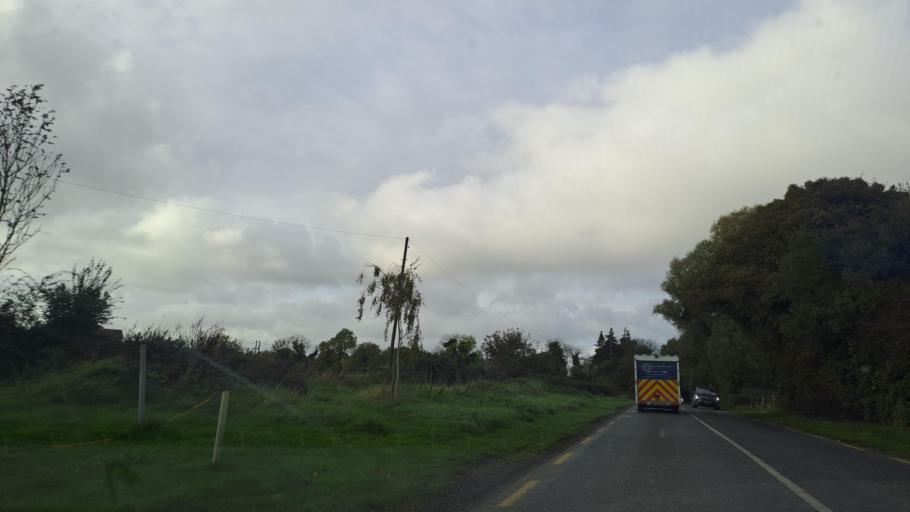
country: IE
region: Leinster
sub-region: An Mhi
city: Navan
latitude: 53.7426
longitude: -6.7159
